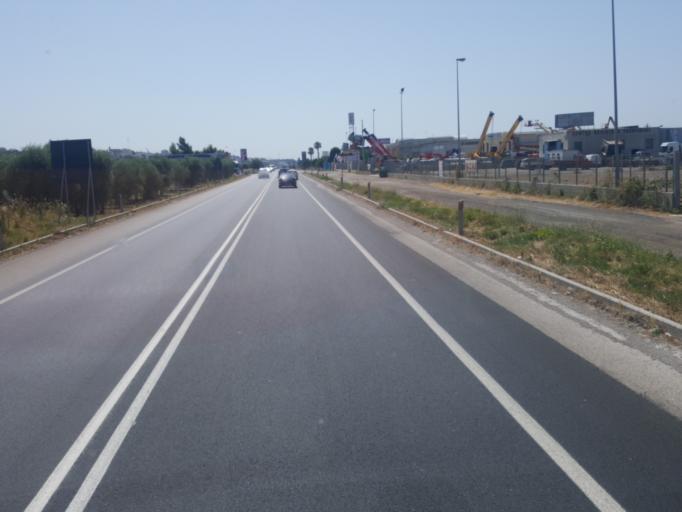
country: IT
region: Apulia
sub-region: Provincia di Taranto
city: Massafra
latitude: 40.5937
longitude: 17.0913
